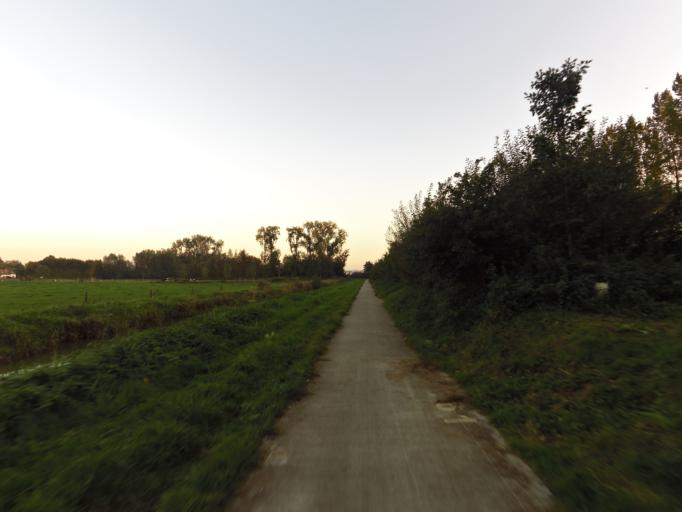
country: NL
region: Gelderland
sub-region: Gemeente Doetinchem
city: Doetinchem
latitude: 51.9272
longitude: 6.3308
